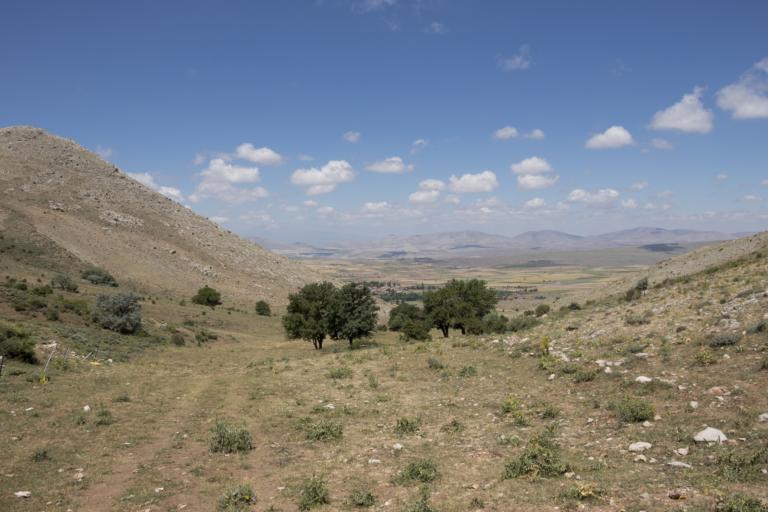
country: TR
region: Kayseri
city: Toklar
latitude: 38.4153
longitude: 36.1144
